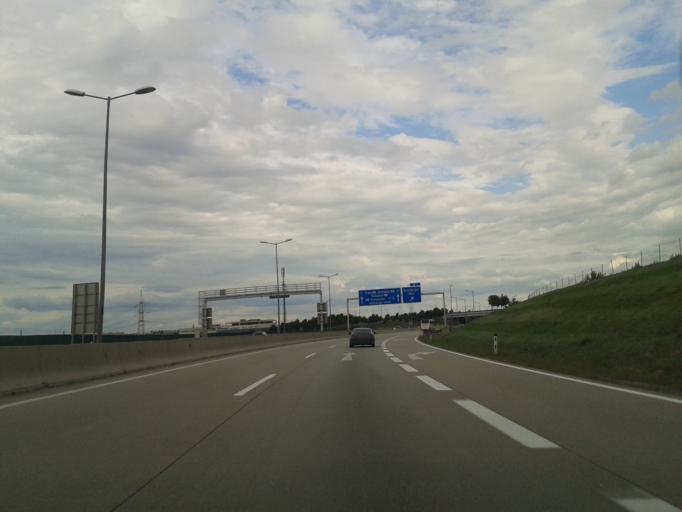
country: AT
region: Lower Austria
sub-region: Politischer Bezirk Modling
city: Vosendorf
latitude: 48.1311
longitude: 16.3356
